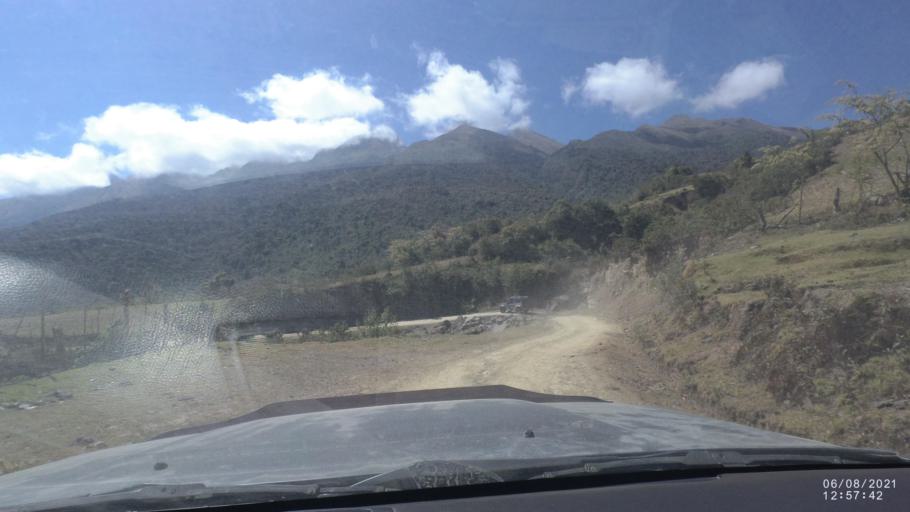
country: BO
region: Cochabamba
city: Colchani
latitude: -16.7532
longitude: -66.6874
